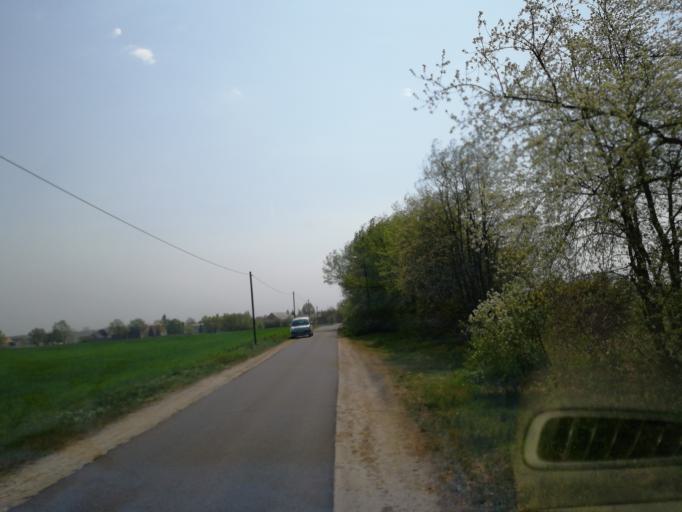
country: DE
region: Brandenburg
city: Sallgast
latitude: 51.6452
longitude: 13.8602
